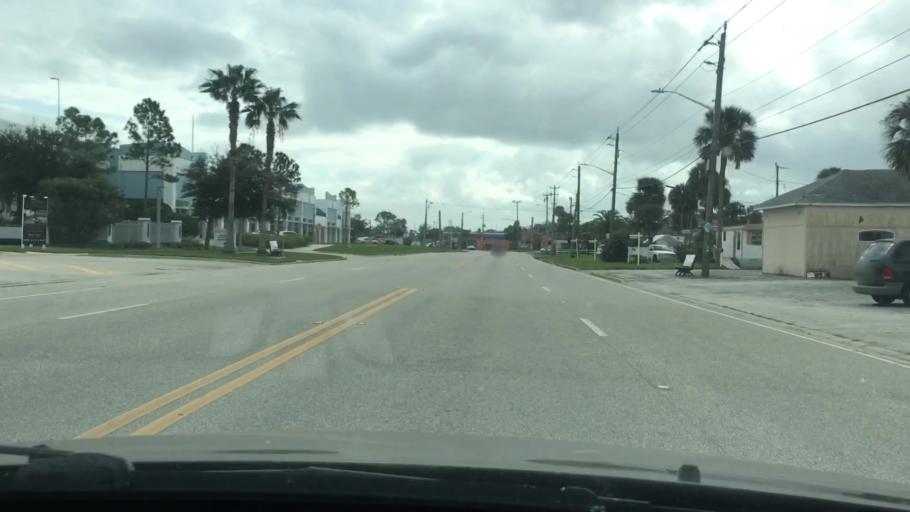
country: US
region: Florida
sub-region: Volusia County
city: Holly Hill
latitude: 29.2328
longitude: -81.0295
